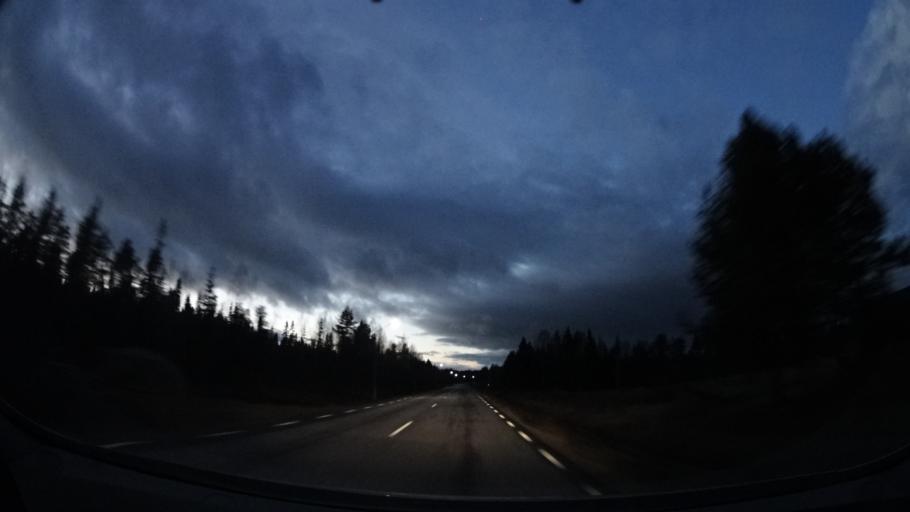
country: SE
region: Vaesterbotten
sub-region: Dorotea Kommun
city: Dorotea
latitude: 64.2432
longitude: 16.6906
